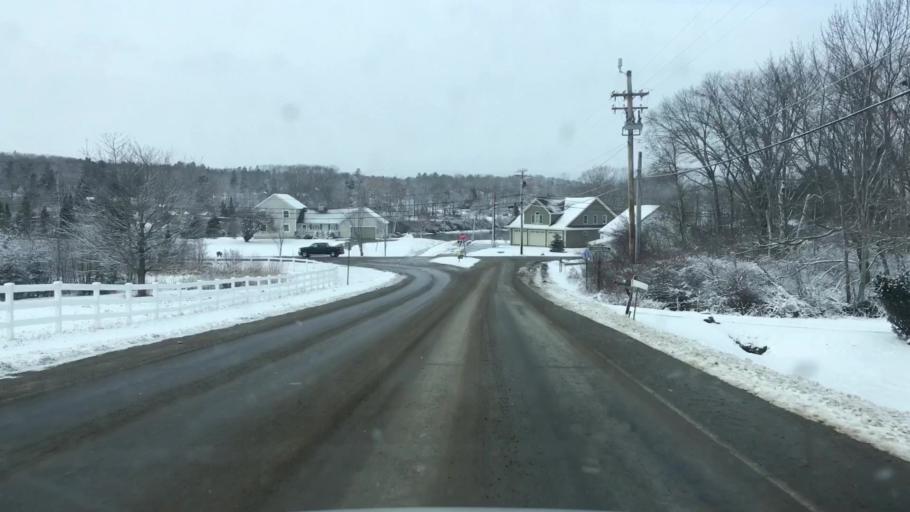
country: US
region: Maine
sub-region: Knox County
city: Rockland
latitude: 44.0760
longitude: -69.1014
